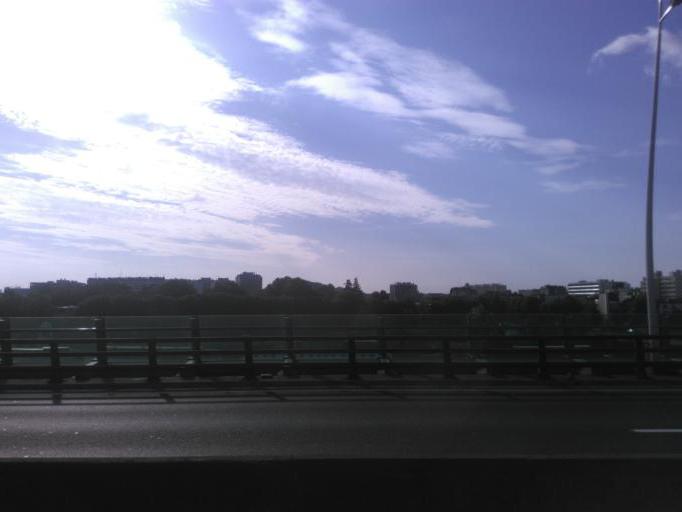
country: FR
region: Ile-de-France
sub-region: Departement des Hauts-de-Seine
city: Saint-Cloud
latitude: 48.8429
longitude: 2.2224
